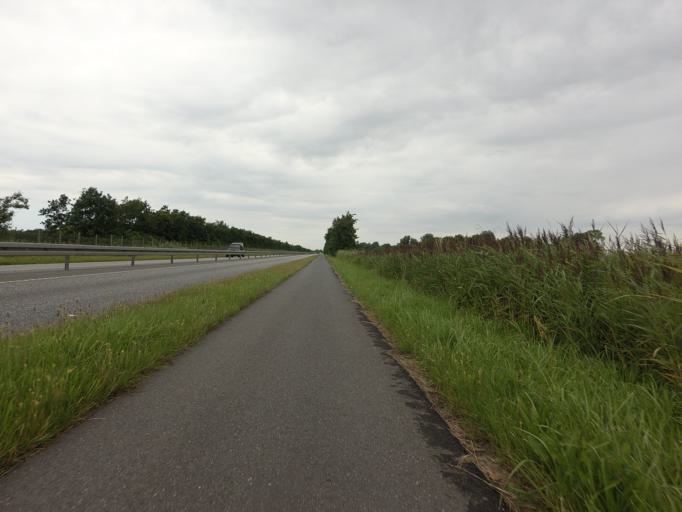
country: DK
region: North Denmark
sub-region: Alborg Kommune
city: Vadum
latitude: 57.0868
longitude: 9.8887
